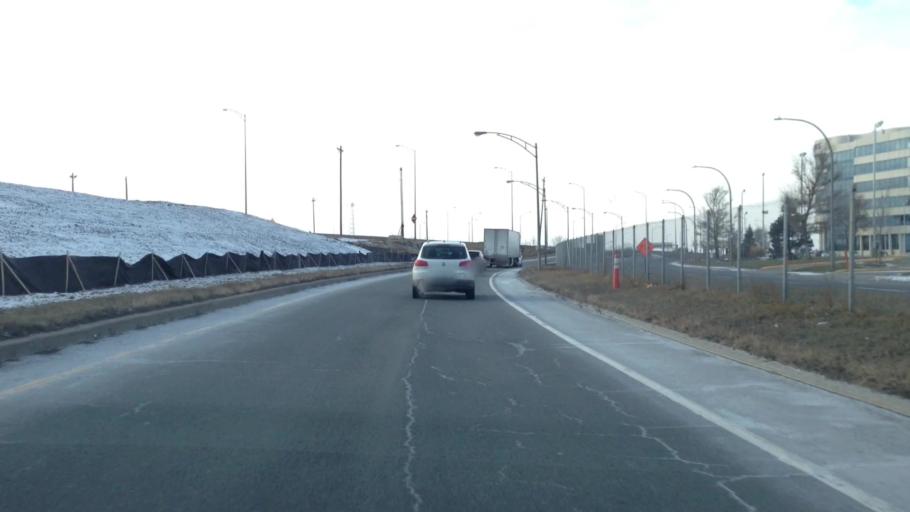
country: CA
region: Quebec
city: Dorval
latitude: 45.4914
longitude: -73.7359
